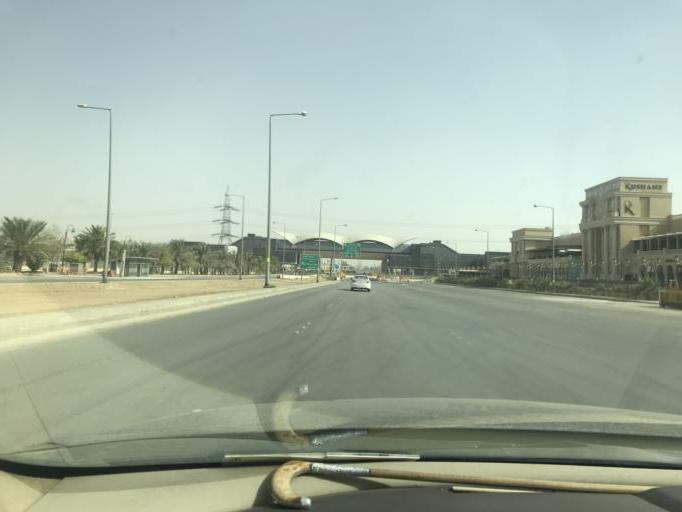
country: SA
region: Ar Riyad
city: Riyadh
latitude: 24.8043
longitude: 46.6945
